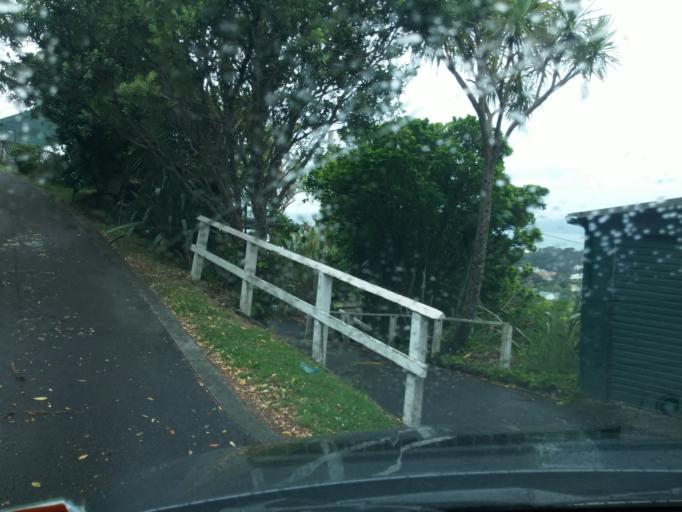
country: NZ
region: Wellington
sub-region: Wellington City
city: Kelburn
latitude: -41.2864
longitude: 174.7558
